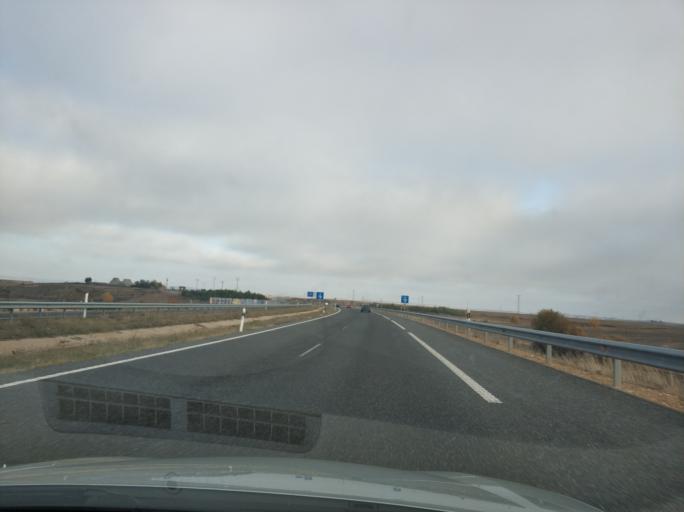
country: ES
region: Castille and Leon
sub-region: Provincia de Leon
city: Valdefresno
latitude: 42.5617
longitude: -5.5007
